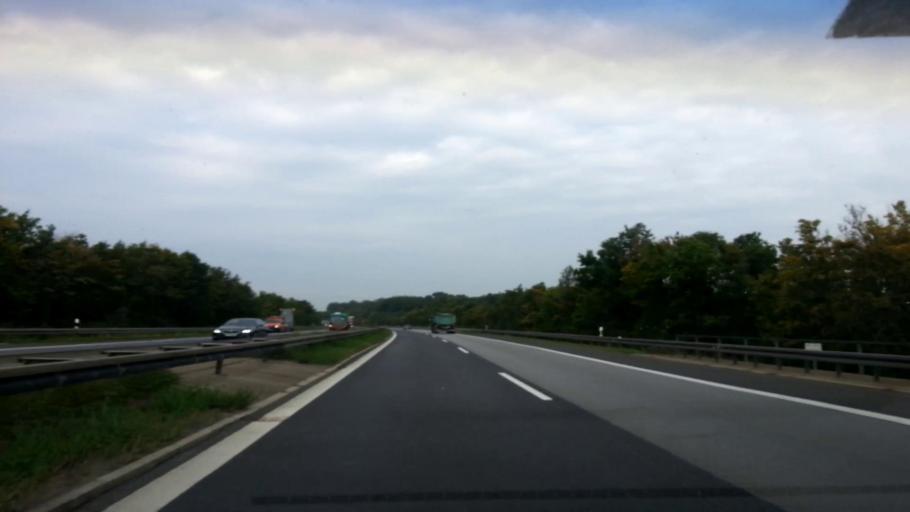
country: DE
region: Bavaria
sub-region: Regierungsbezirk Unterfranken
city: Hassfurt
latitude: 49.9989
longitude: 10.5163
